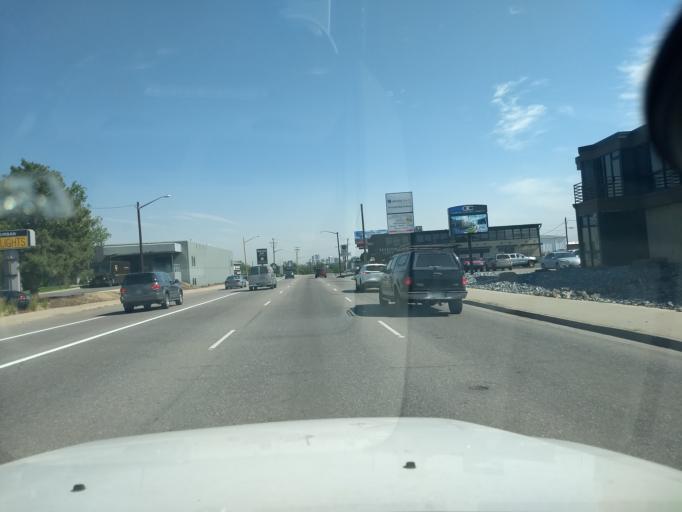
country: US
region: Colorado
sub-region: Arapahoe County
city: Englewood
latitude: 39.6916
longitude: -104.9924
